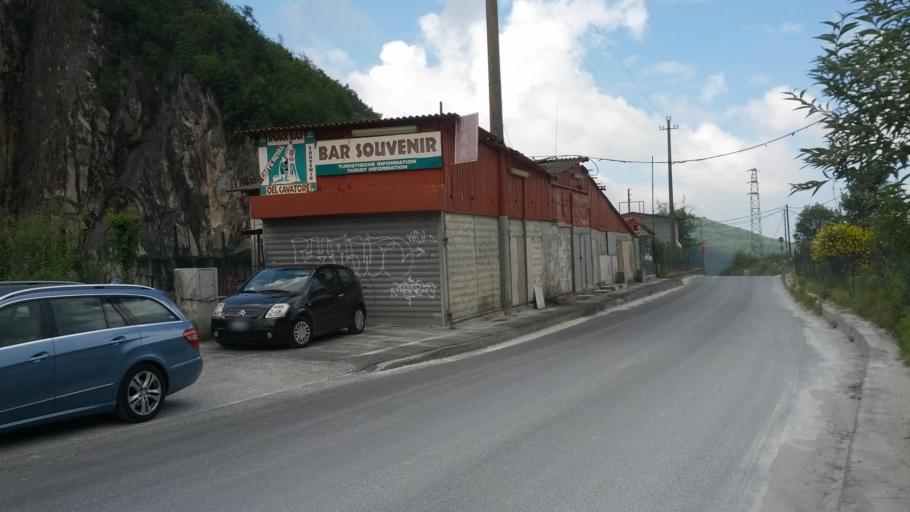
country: IT
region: Tuscany
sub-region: Provincia di Massa-Carrara
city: Montignoso
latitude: 44.0822
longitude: 10.1464
